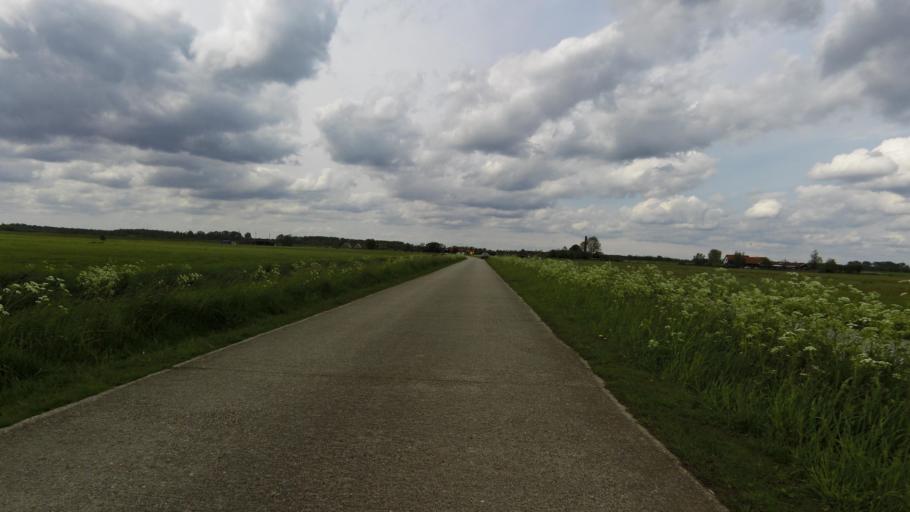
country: NL
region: Gelderland
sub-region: Gemeente Nijkerk
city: Nijkerk
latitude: 52.2580
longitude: 5.4959
